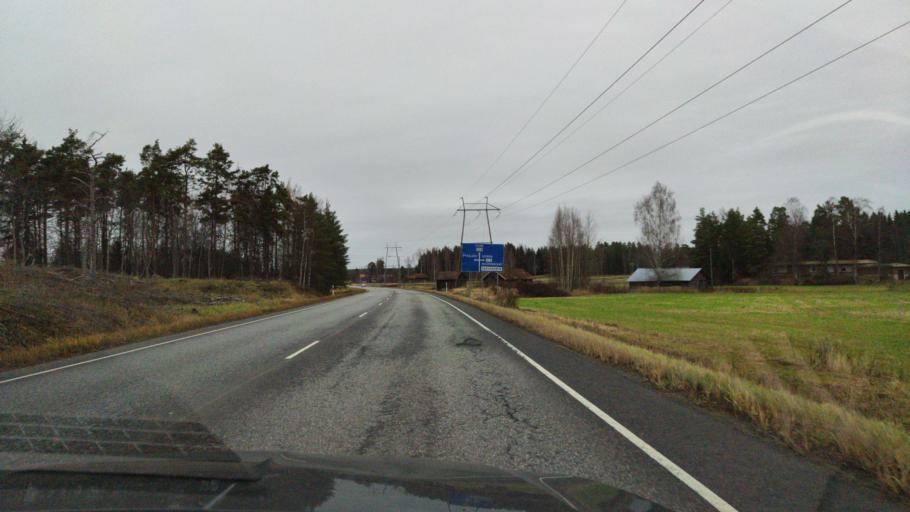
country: FI
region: Satakunta
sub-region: Rauma
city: Saekylae
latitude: 61.0181
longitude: 22.4102
